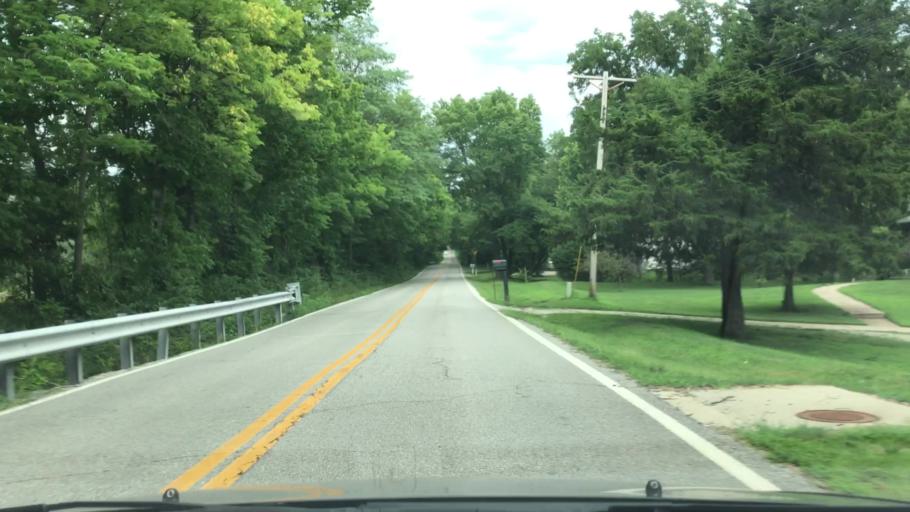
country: US
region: Missouri
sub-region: Jackson County
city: Lees Summit
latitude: 38.8910
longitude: -94.4397
